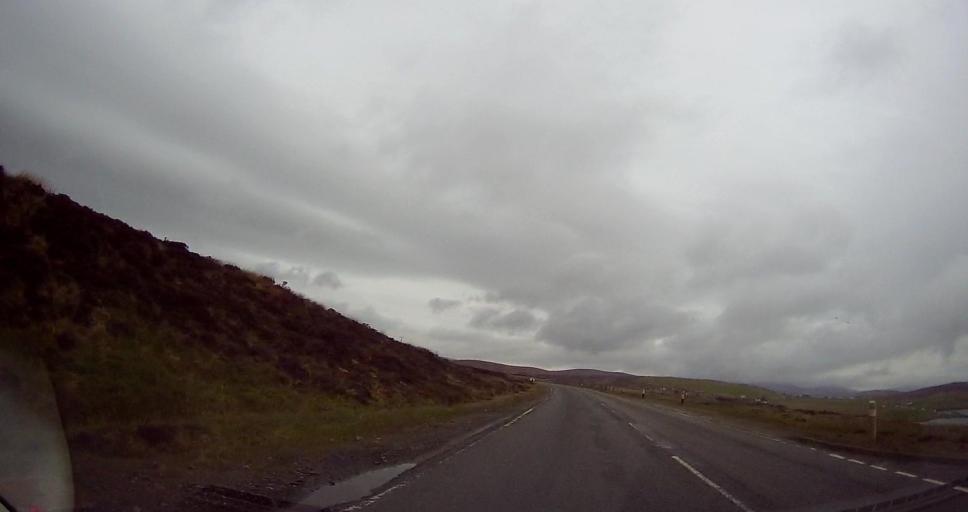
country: GB
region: Scotland
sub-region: Shetland Islands
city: Lerwick
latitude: 60.2239
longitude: -1.2343
